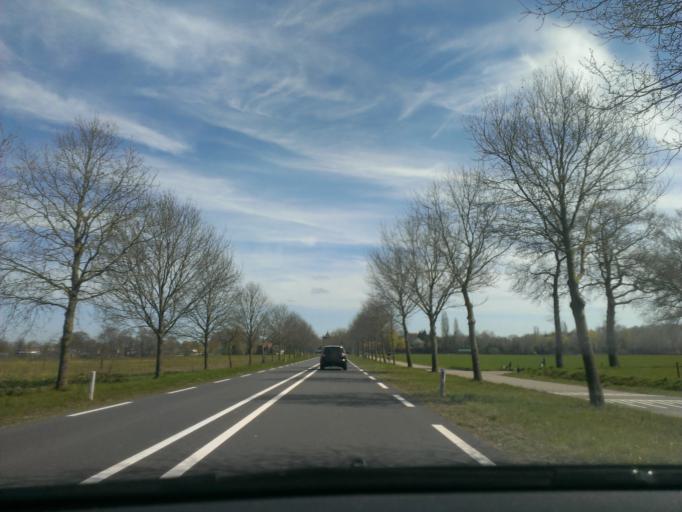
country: NL
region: Overijssel
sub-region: Gemeente Raalte
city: Raalte
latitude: 52.3819
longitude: 6.3126
